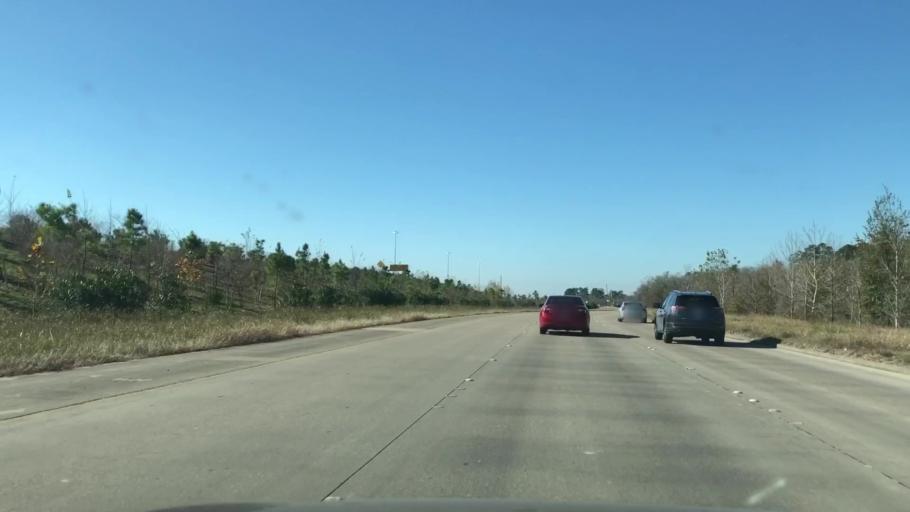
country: US
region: Texas
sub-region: Harris County
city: Cloverleaf
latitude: 29.8323
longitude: -95.1777
